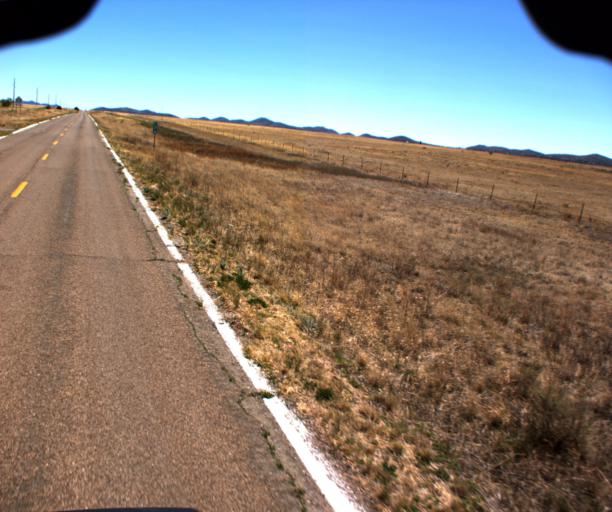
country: US
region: Arizona
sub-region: Cochise County
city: Huachuca City
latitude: 31.6391
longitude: -110.5992
